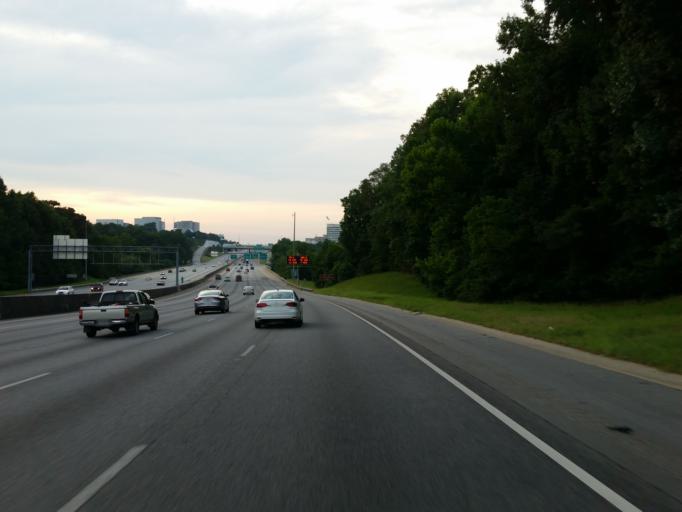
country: US
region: Georgia
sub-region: Cobb County
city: Vinings
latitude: 33.8726
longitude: -84.4445
